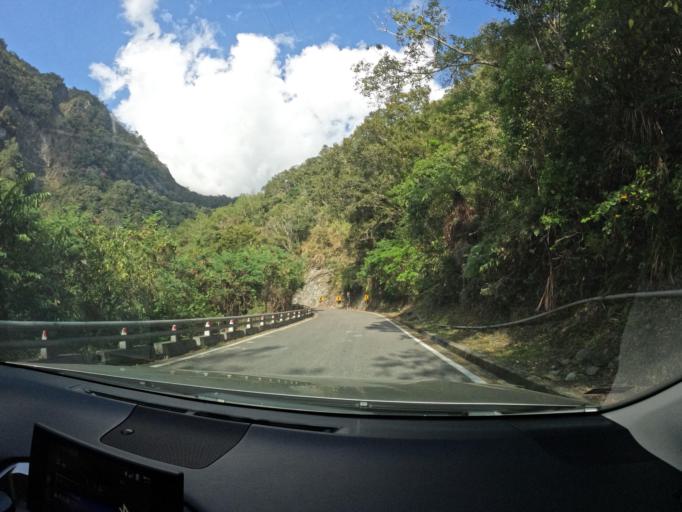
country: TW
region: Taiwan
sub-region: Taitung
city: Taitung
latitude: 23.1722
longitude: 121.0385
